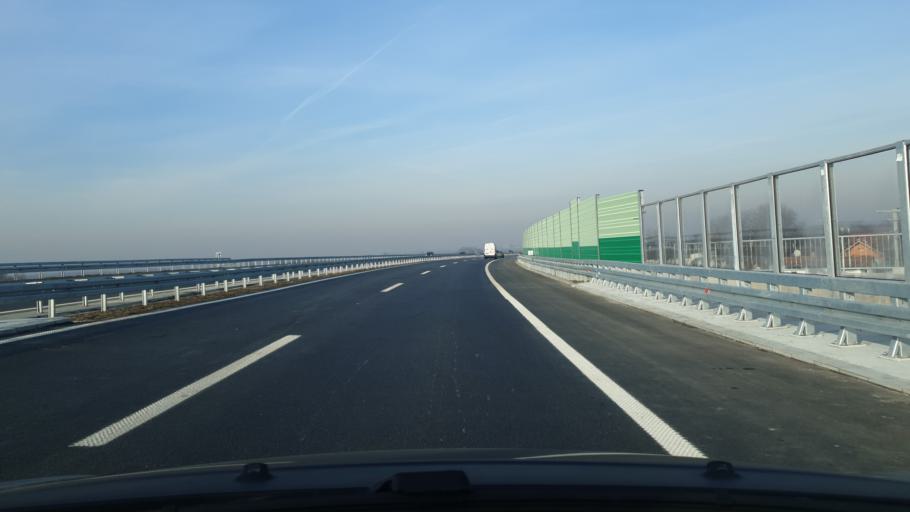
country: RS
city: Boljevci
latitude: 44.7325
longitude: 20.2460
